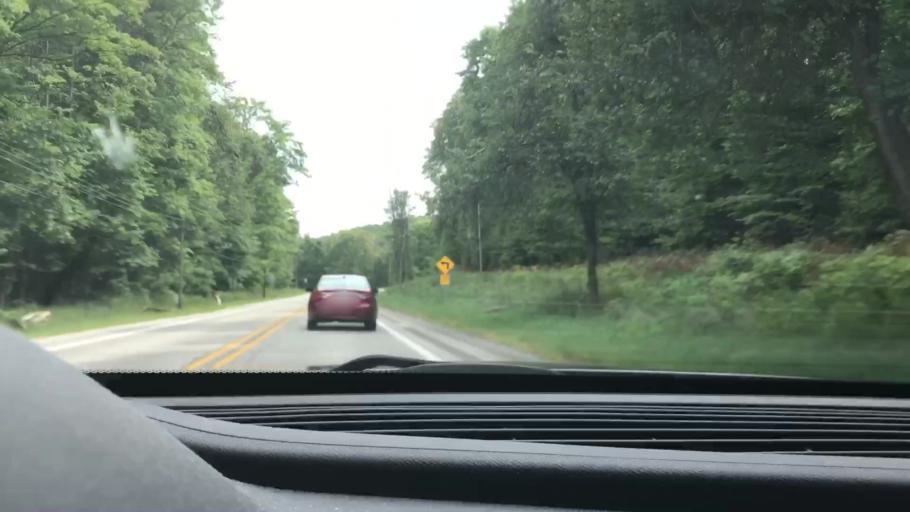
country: US
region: Michigan
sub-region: Antrim County
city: Bellaire
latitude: 45.0811
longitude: -85.2842
